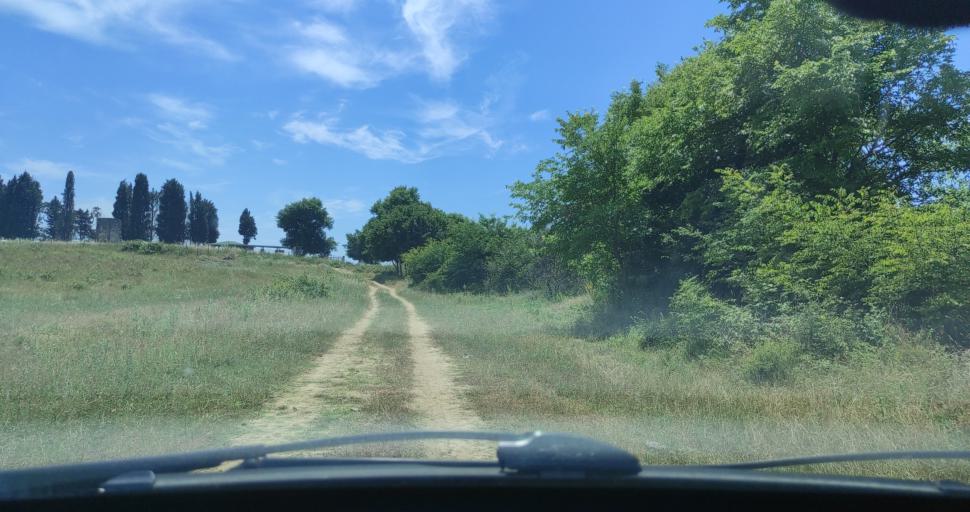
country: AL
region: Shkoder
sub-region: Rrethi i Shkodres
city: Velipoje
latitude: 41.8843
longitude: 19.3846
